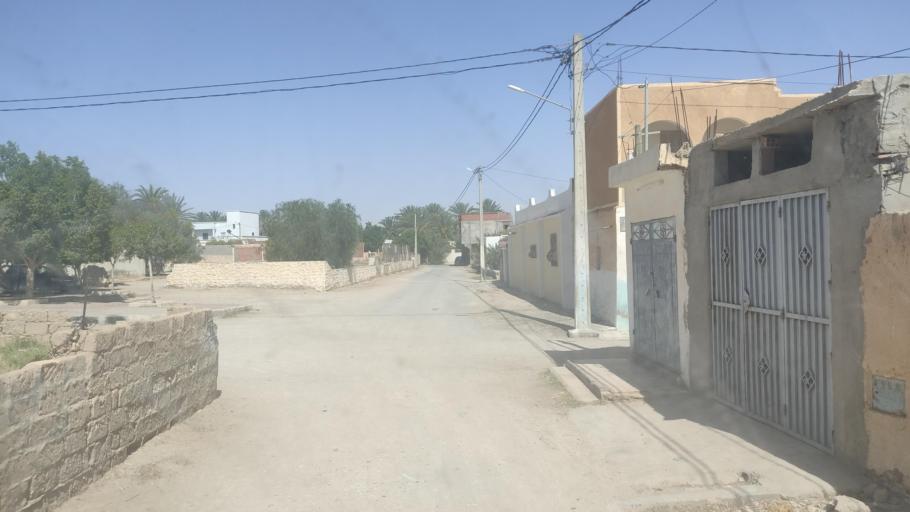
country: TN
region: Gafsa
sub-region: Gafsa Municipality
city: Gafsa
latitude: 34.3356
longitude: 8.9205
